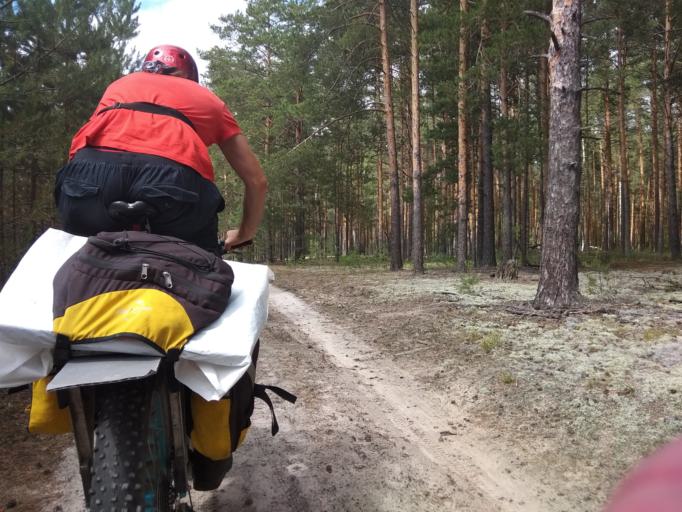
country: RU
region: Moskovskaya
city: Misheronskiy
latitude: 55.6405
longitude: 39.7064
